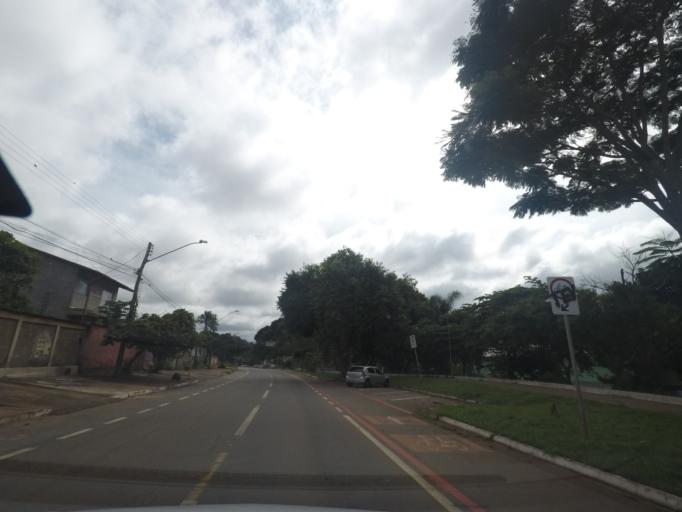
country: BR
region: Goias
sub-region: Goiania
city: Goiania
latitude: -16.7241
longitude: -49.2537
